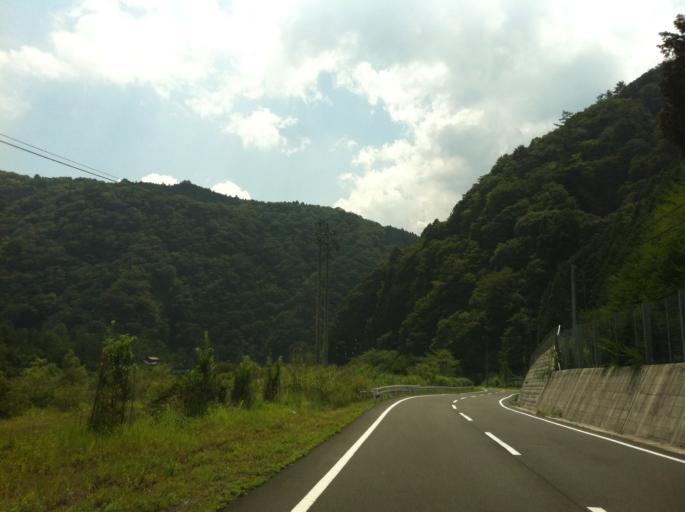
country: JP
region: Shizuoka
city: Fujinomiya
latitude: 35.2832
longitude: 138.3393
